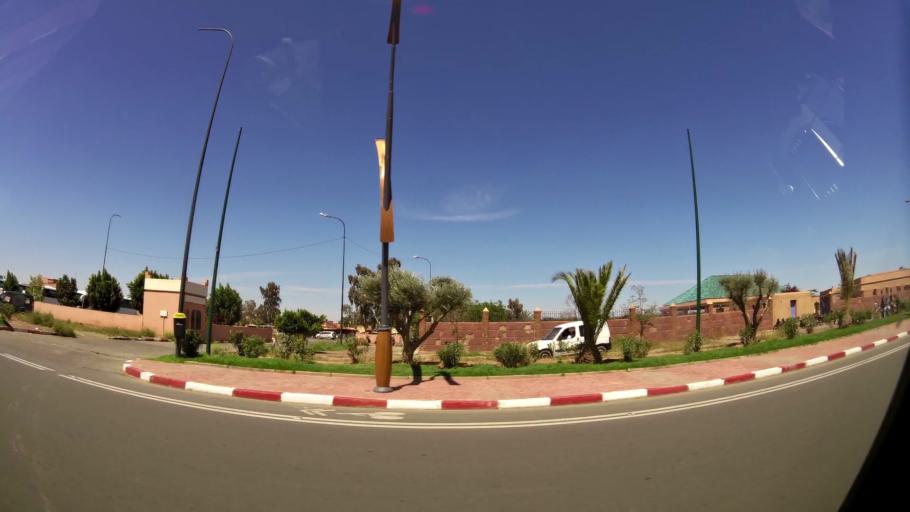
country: MA
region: Marrakech-Tensift-Al Haouz
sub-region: Marrakech
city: Marrakesh
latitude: 31.6064
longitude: -7.9976
